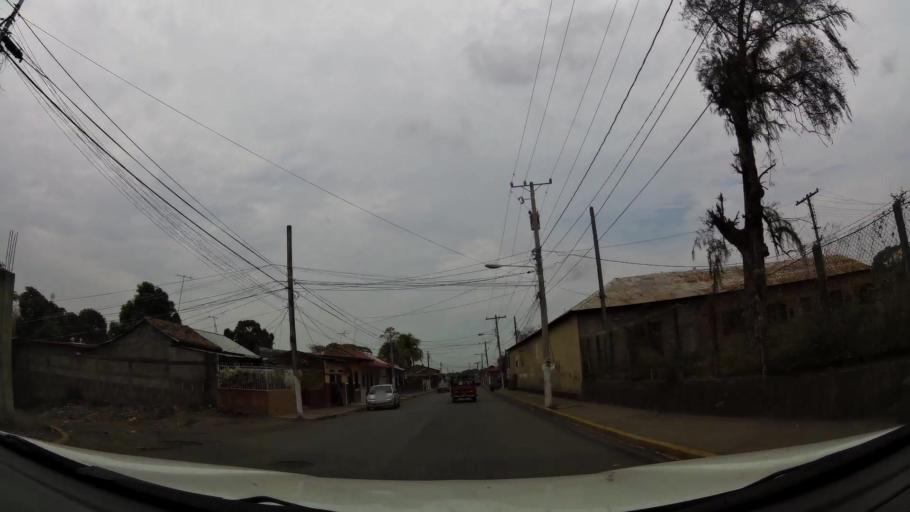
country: NI
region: Granada
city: Granada
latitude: 11.9239
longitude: -85.9581
